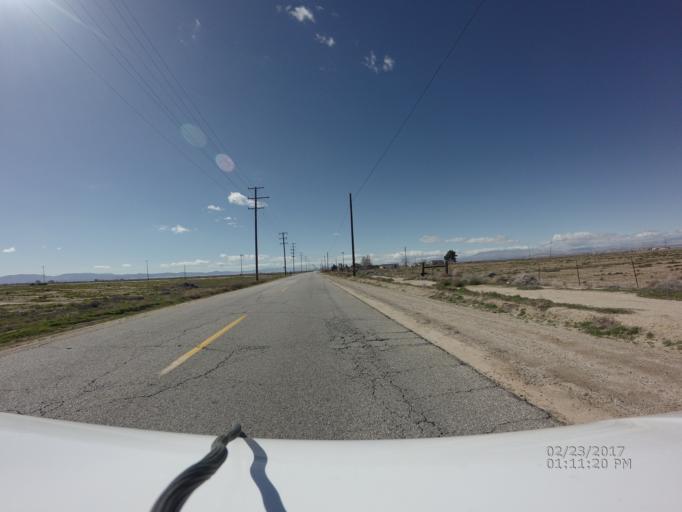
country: US
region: California
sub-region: Los Angeles County
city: Lancaster
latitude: 34.7631
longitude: -118.0219
